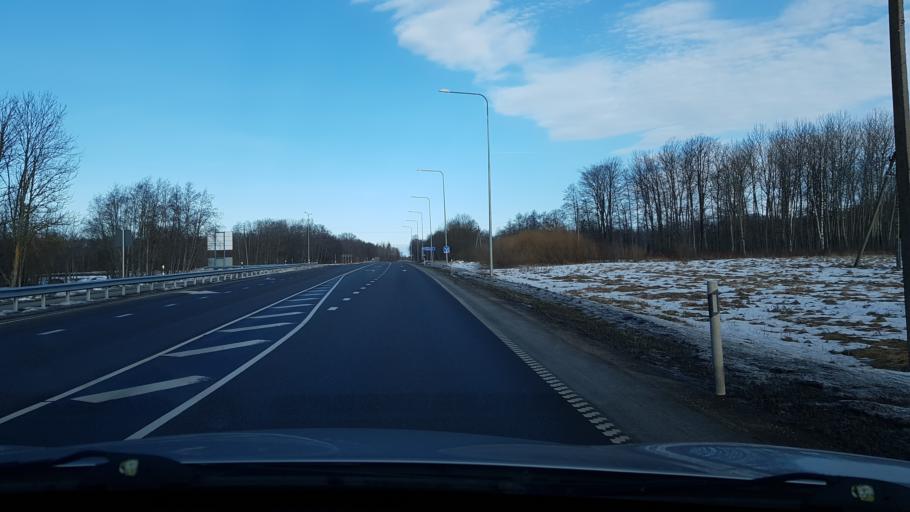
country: EE
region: Viljandimaa
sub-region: Viljandi linn
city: Viljandi
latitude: 58.3756
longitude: 25.5631
